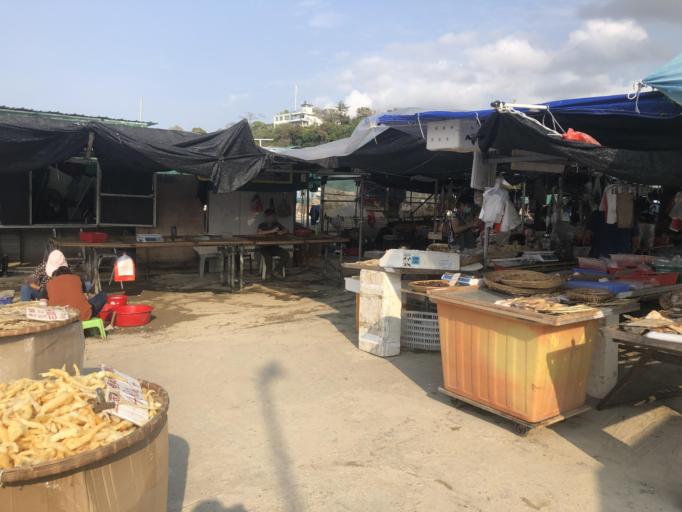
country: HK
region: Yuen Long
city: Yuen Long Kau Hui
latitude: 22.4688
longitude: 113.9814
